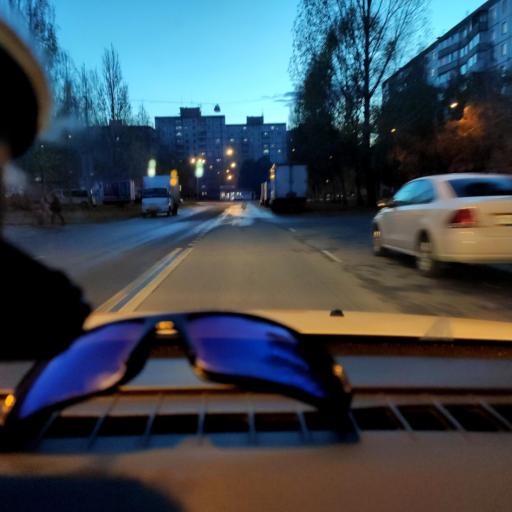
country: RU
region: Samara
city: Samara
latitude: 53.2620
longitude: 50.2307
